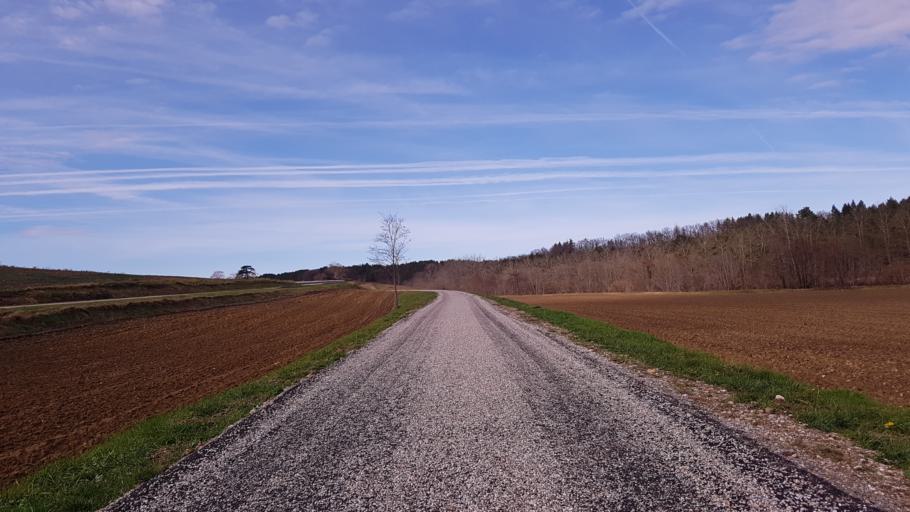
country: FR
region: Languedoc-Roussillon
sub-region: Departement de l'Aude
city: Chalabre
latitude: 42.9536
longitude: 1.9858
